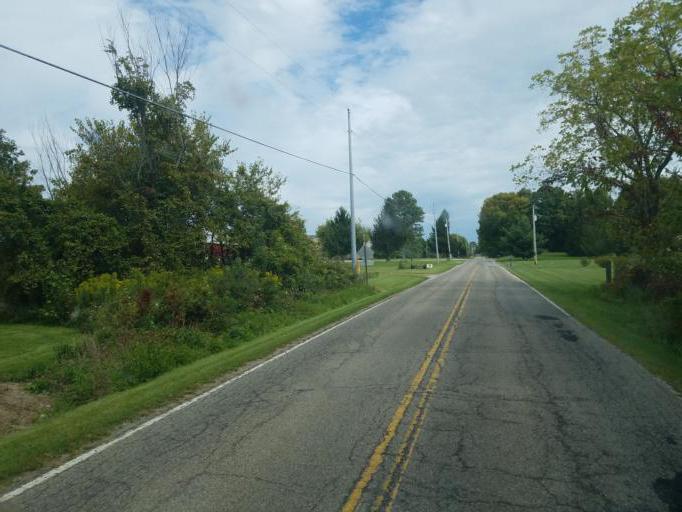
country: US
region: Ohio
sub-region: Licking County
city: Johnstown
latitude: 40.0958
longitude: -82.7219
